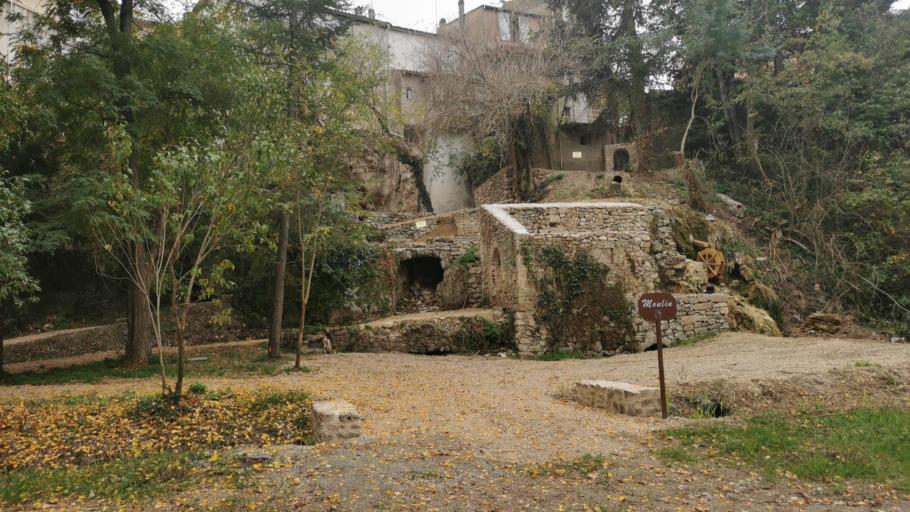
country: FR
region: Provence-Alpes-Cote d'Azur
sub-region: Departement du Vaucluse
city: Beaumont-de-Pertuis
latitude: 43.6878
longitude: 5.7089
